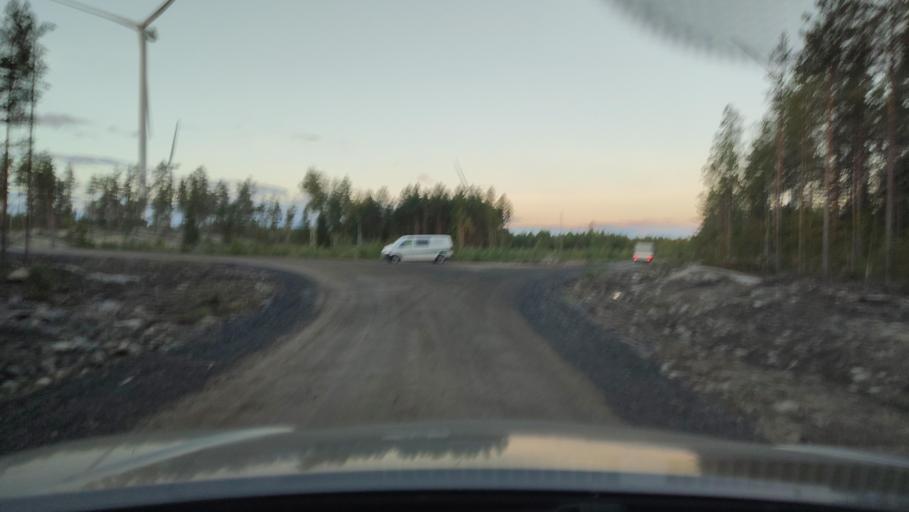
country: FI
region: Southern Ostrobothnia
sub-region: Suupohja
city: Karijoki
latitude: 62.1912
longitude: 21.5746
